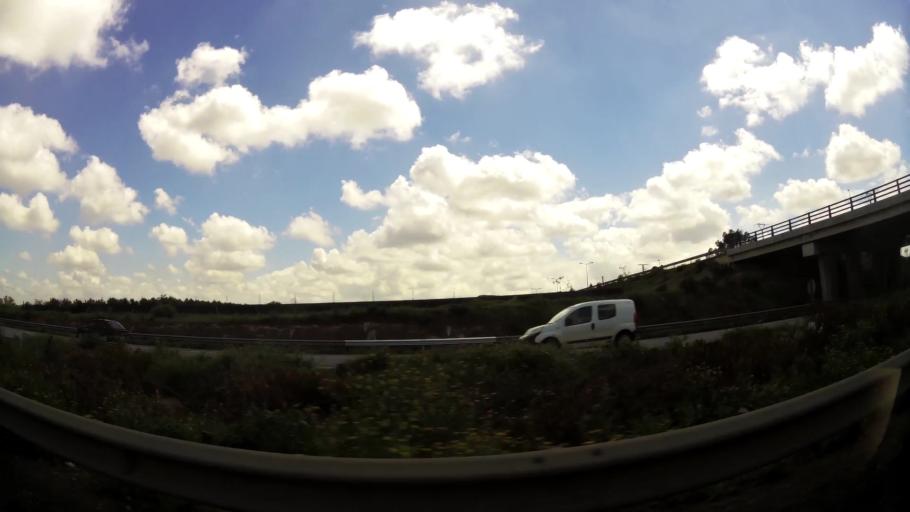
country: MA
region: Grand Casablanca
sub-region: Nouaceur
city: Bouskoura
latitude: 33.5075
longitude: -7.6157
